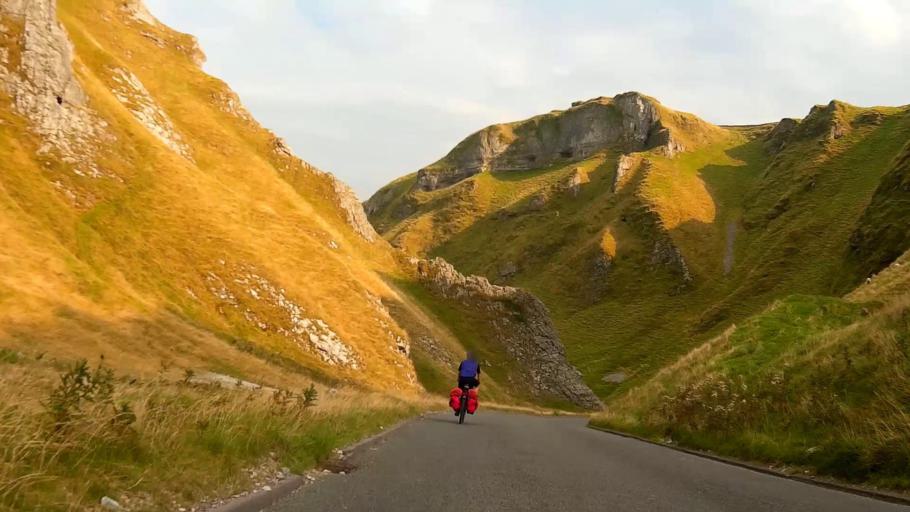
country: GB
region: England
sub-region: Derbyshire
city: High Peak
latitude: 53.3407
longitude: -1.7991
